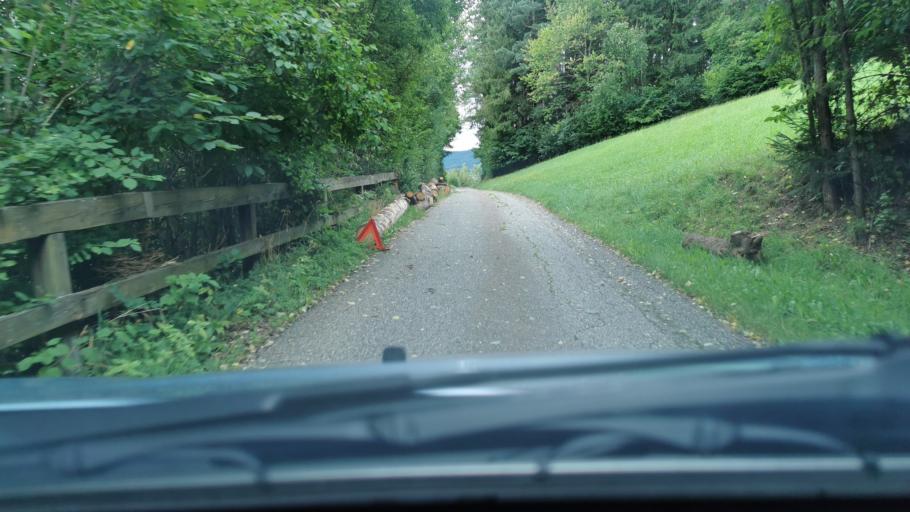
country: AT
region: Styria
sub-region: Politischer Bezirk Weiz
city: Birkfeld
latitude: 47.3597
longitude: 15.6956
